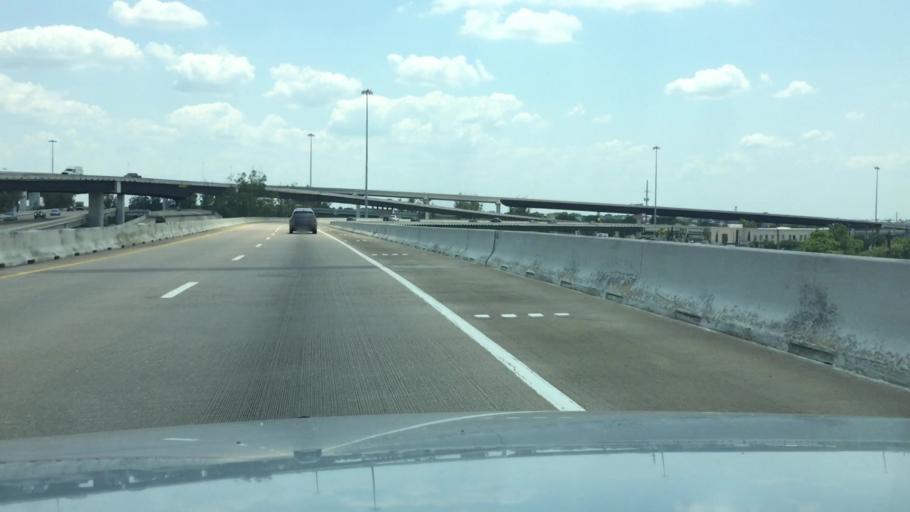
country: US
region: Texas
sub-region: Fort Bend County
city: Meadows Place
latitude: 29.6636
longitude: -95.5597
